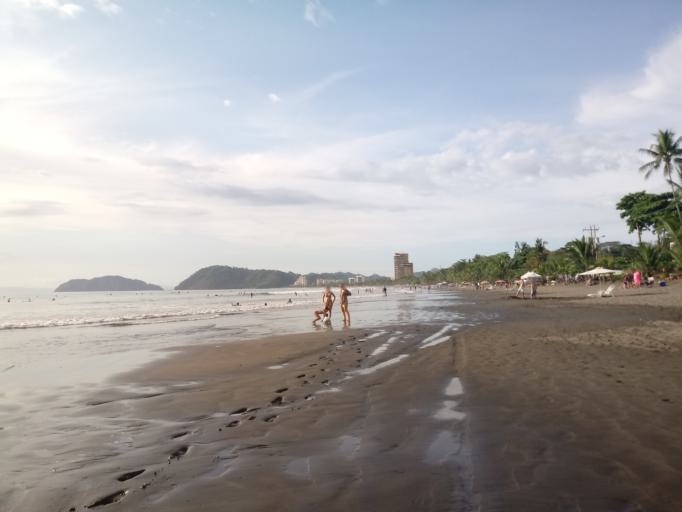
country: CR
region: Puntarenas
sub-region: Canton de Garabito
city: Jaco
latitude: 9.6013
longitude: -84.6210
